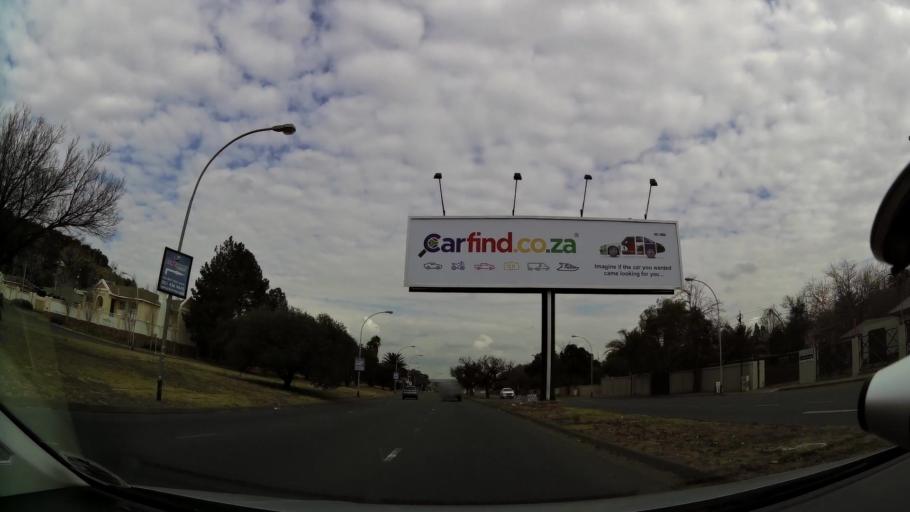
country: ZA
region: Orange Free State
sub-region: Mangaung Metropolitan Municipality
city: Bloemfontein
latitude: -29.0988
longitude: 26.2231
